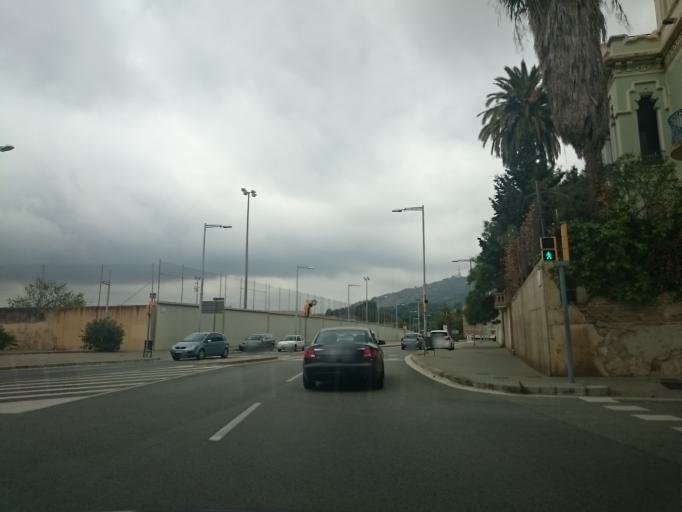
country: ES
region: Catalonia
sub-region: Provincia de Barcelona
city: Sarria-Sant Gervasi
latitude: 41.4060
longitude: 2.1201
